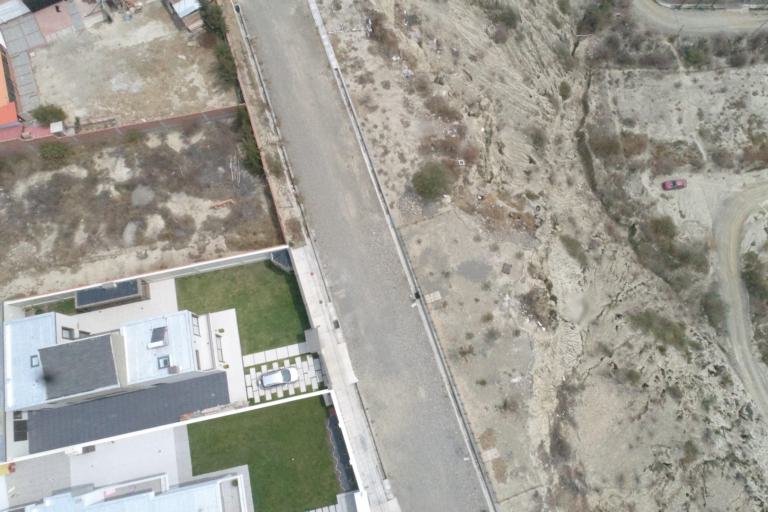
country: BO
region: La Paz
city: La Paz
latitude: -16.6006
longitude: -68.0696
